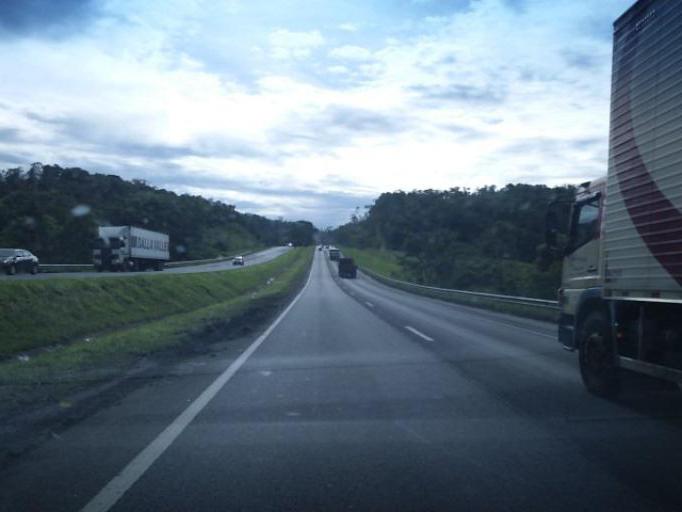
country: BR
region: Parana
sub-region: Antonina
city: Antonina
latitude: -25.1036
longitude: -48.7086
